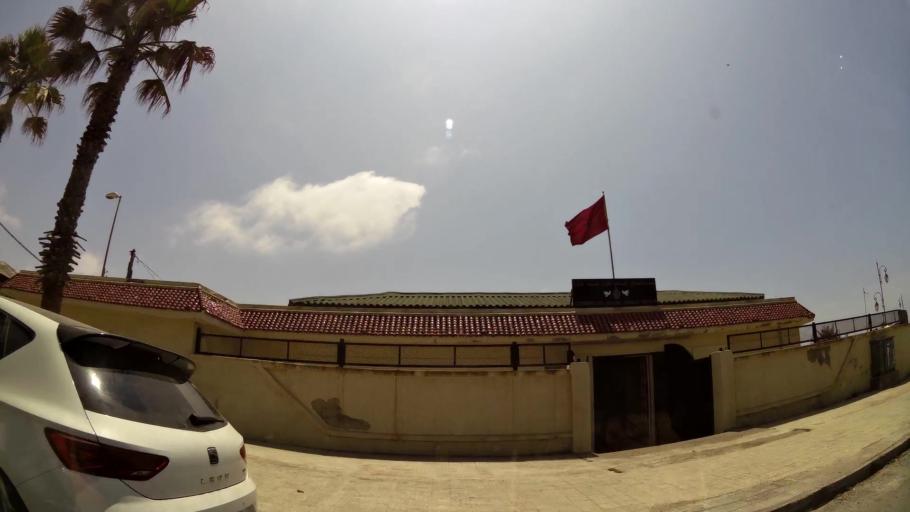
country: MA
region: Rabat-Sale-Zemmour-Zaer
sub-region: Rabat
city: Rabat
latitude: 34.0180
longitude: -6.8572
